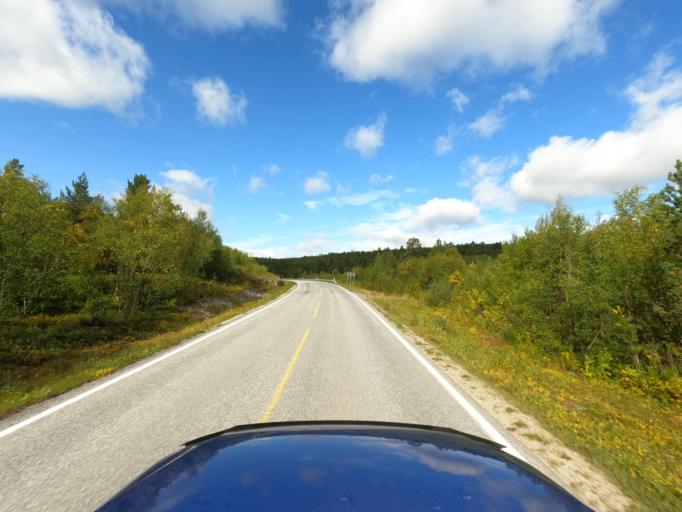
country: NO
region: Finnmark Fylke
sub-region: Karasjok
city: Karasjohka
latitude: 69.4879
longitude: 25.5039
